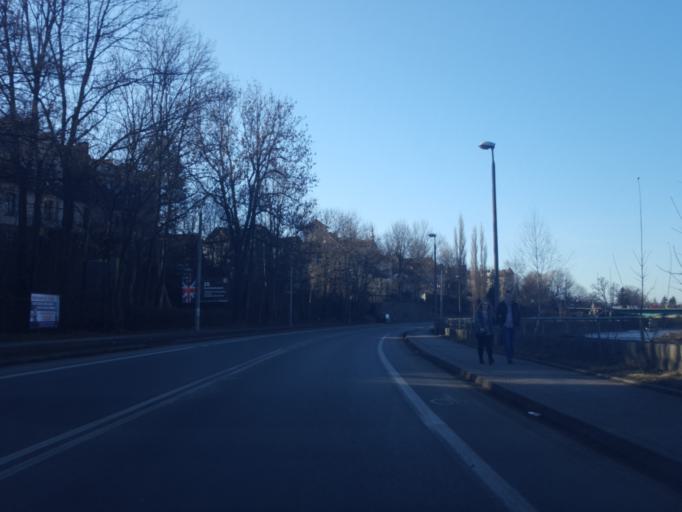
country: PL
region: Lesser Poland Voivodeship
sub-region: Powiat nowosadecki
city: Nowy Sacz
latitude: 49.6223
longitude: 20.6974
